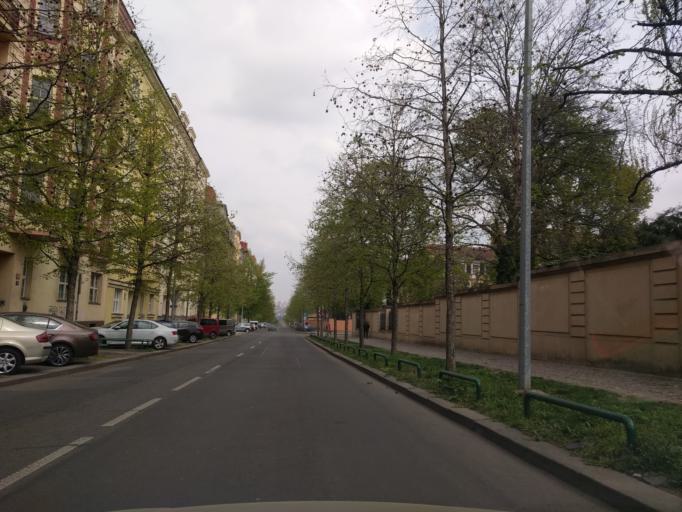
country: CZ
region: Praha
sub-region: Praha 1
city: Mala Strana
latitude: 50.1003
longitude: 14.4044
